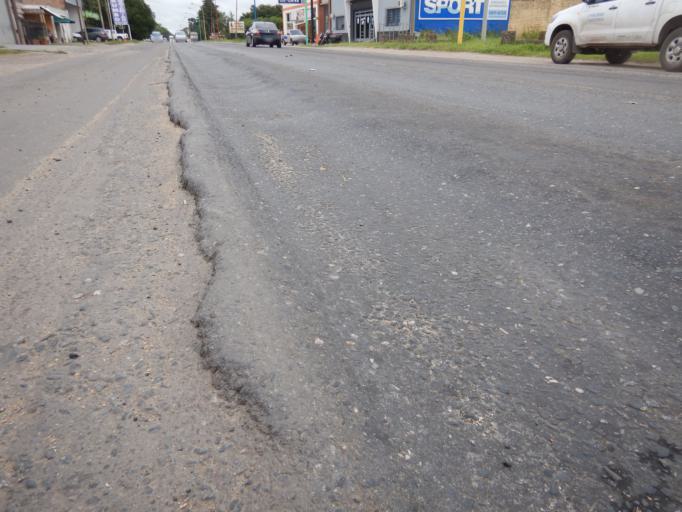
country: AR
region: Santa Fe
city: Canada de Gomez
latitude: -32.8092
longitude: -61.4014
